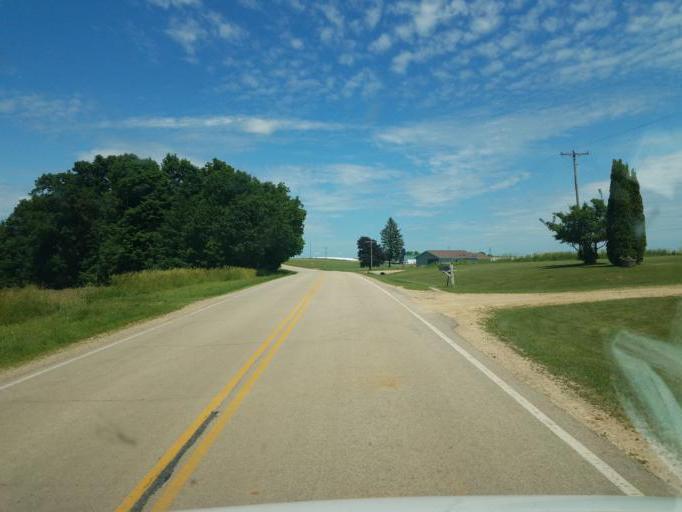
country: US
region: Wisconsin
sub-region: Vernon County
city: Hillsboro
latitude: 43.5963
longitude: -90.2922
